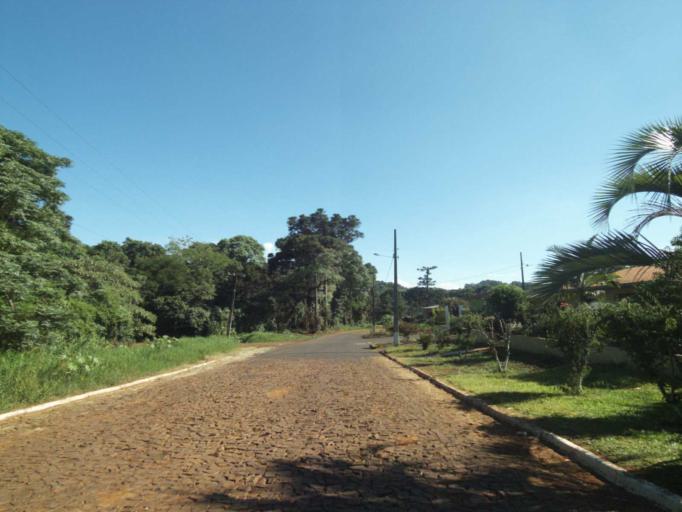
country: BR
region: Parana
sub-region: Laranjeiras Do Sul
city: Laranjeiras do Sul
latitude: -25.3834
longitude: -52.2021
